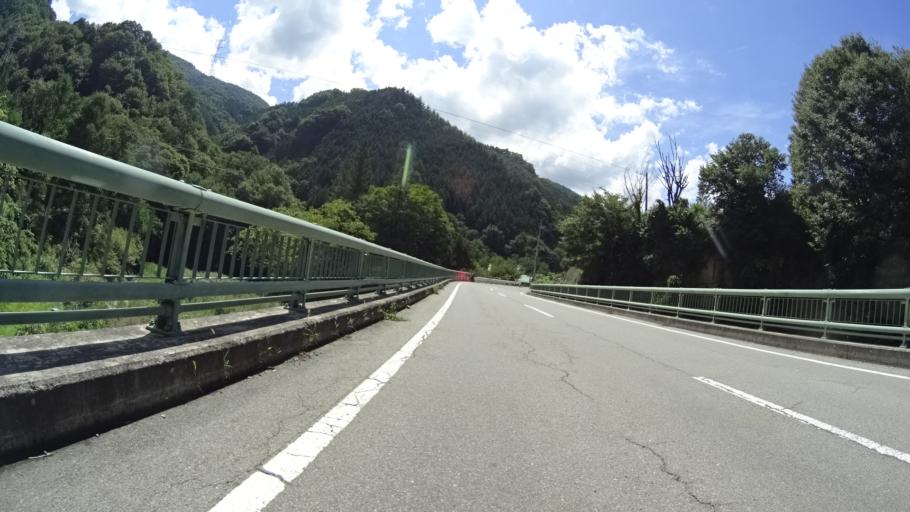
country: JP
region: Yamanashi
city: Enzan
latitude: 35.6406
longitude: 138.7996
